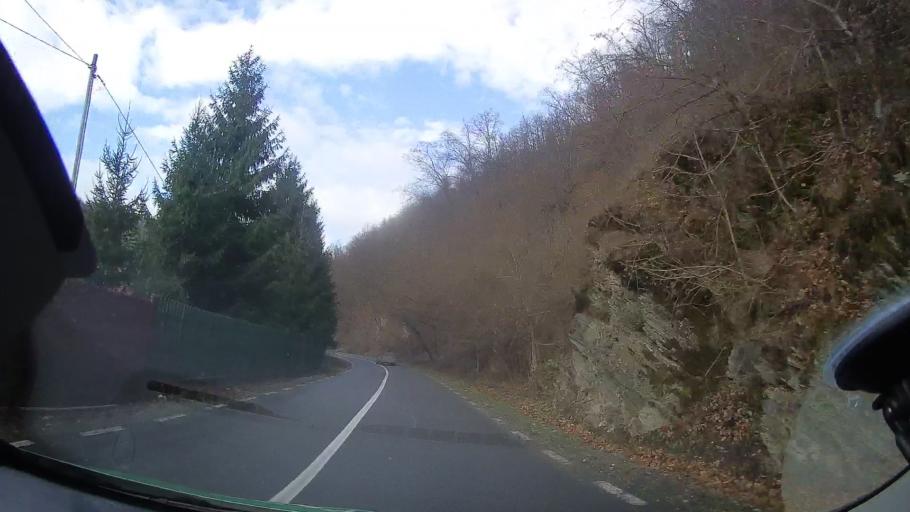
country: RO
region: Cluj
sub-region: Comuna Valea Ierii
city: Valea Ierii
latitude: 46.6138
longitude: 23.4052
